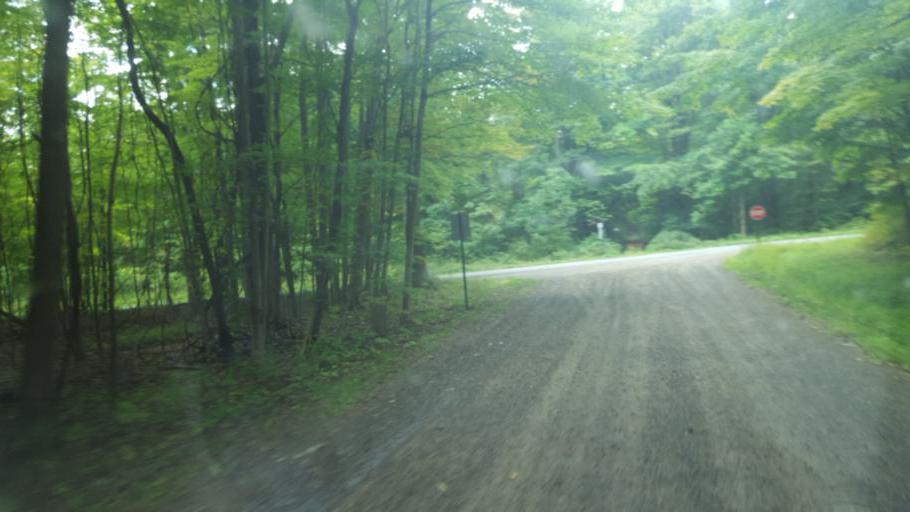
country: US
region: Pennsylvania
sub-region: Crawford County
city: Pymatuning Central
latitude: 41.5169
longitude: -80.3969
